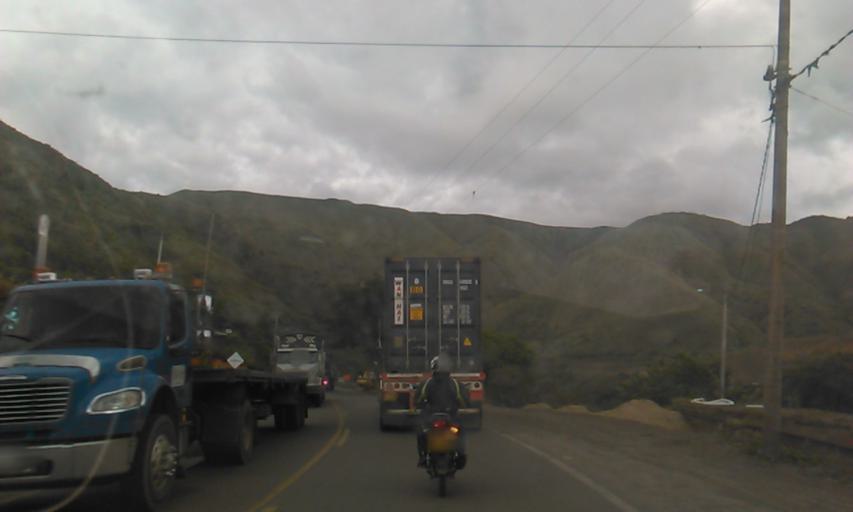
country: CO
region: Valle del Cauca
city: Dagua
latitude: 3.7607
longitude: -76.6631
